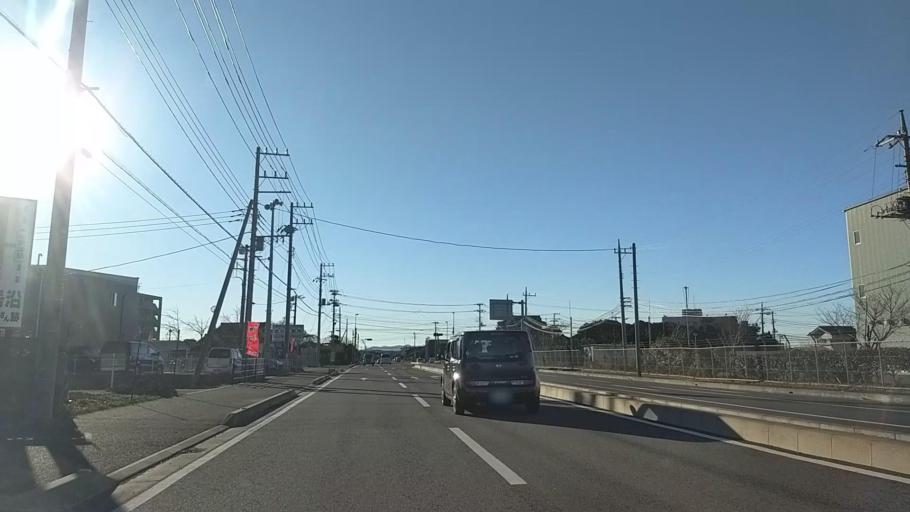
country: JP
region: Chiba
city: Kisarazu
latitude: 35.4044
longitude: 139.9190
